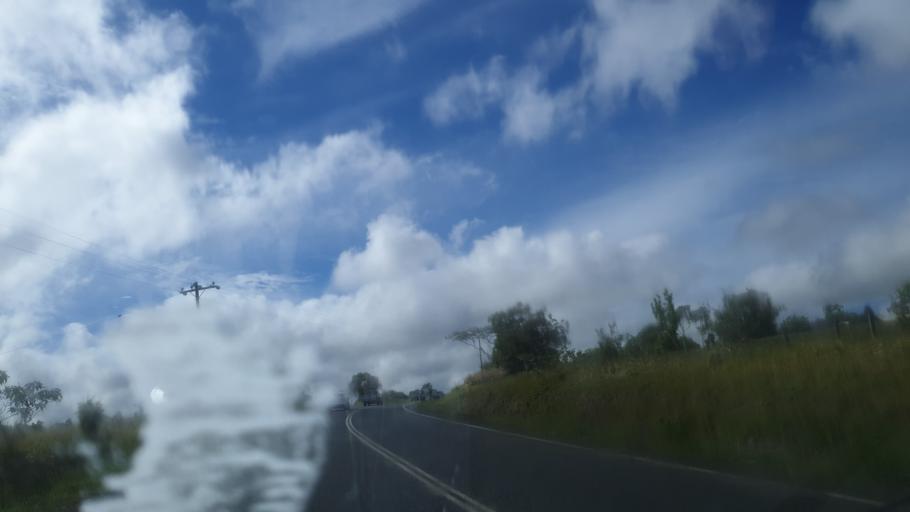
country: AU
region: Queensland
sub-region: Tablelands
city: Atherton
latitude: -17.3468
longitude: 145.5795
